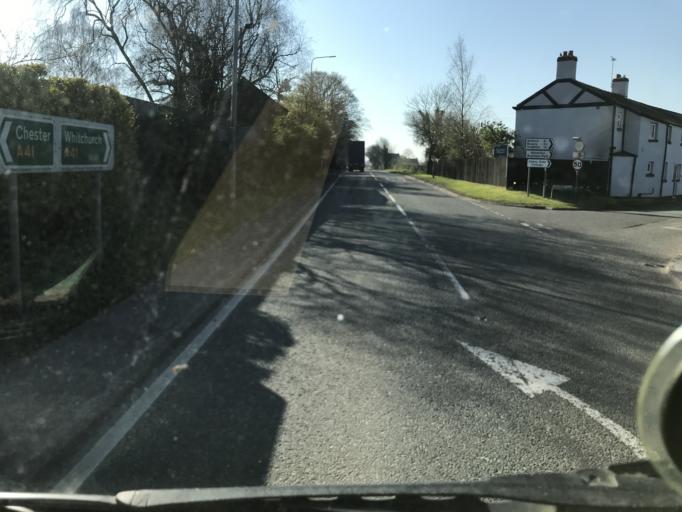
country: GB
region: England
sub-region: Cheshire West and Chester
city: Waverton
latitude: 53.1693
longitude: -2.8211
